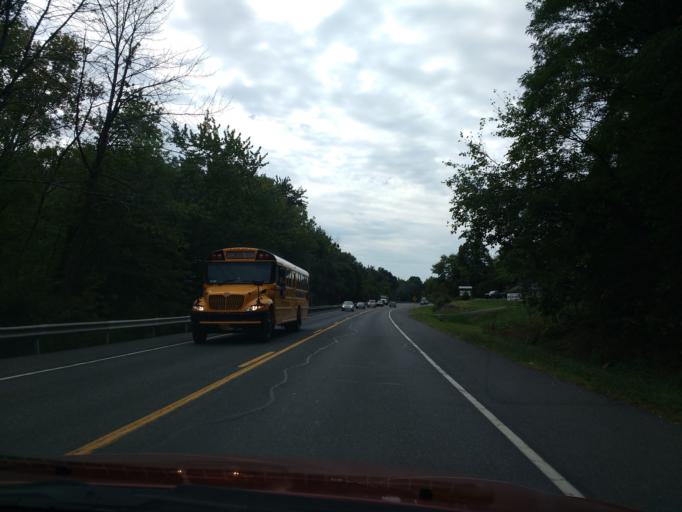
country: US
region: New York
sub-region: Ulster County
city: Lincoln Park
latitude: 41.9478
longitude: -73.9803
